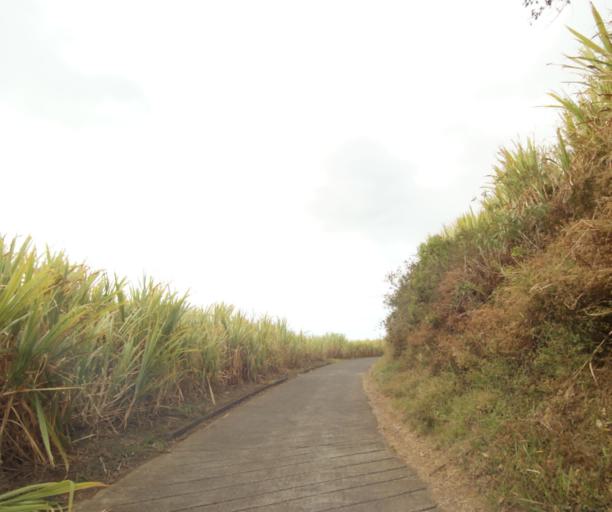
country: RE
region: Reunion
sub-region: Reunion
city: Saint-Paul
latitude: -21.0245
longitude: 55.3221
